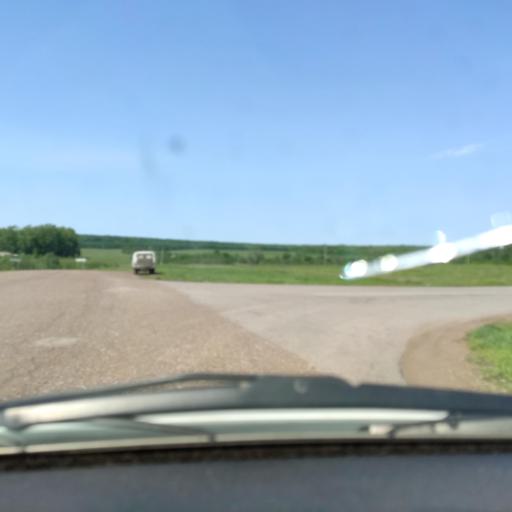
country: RU
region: Bashkortostan
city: Chishmy
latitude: 54.4739
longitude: 55.5416
